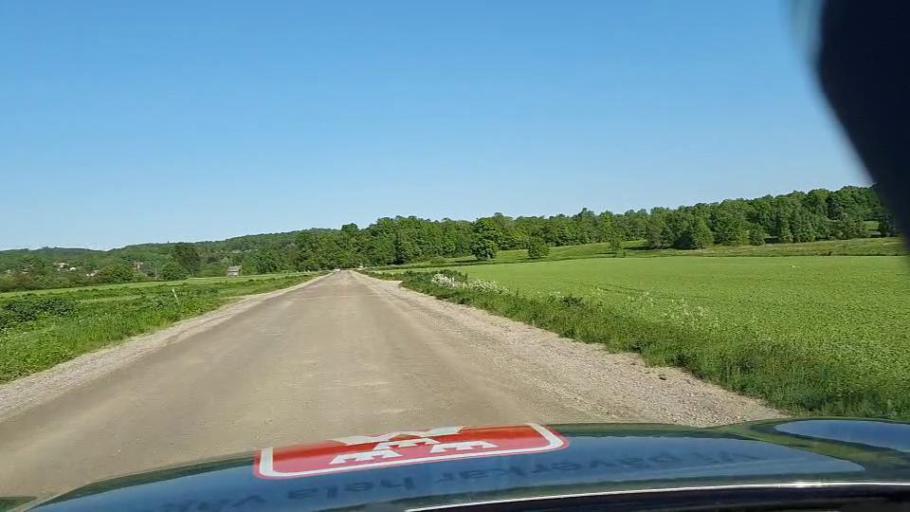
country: SE
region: Skane
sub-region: Hassleholms Kommun
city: Tormestorp
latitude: 56.1129
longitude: 13.7238
